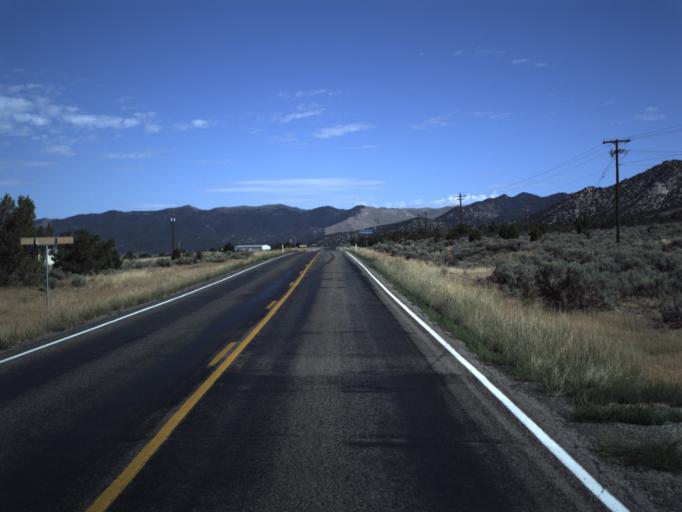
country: US
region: Utah
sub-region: Juab County
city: Mona
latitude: 39.9143
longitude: -112.1425
